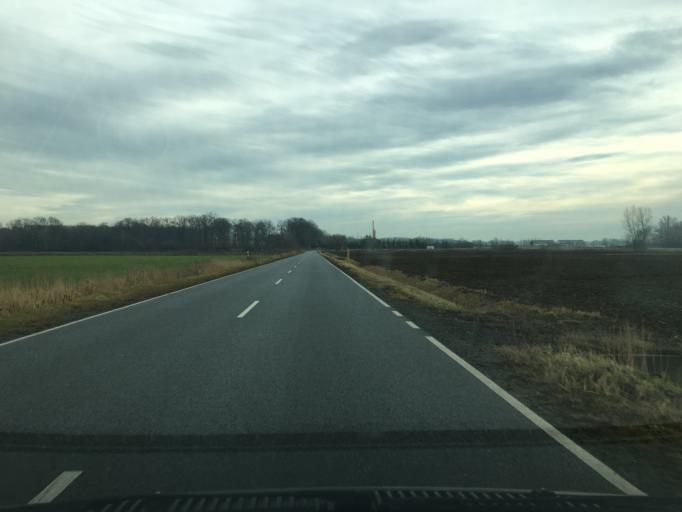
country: PL
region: Lower Silesian Voivodeship
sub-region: Powiat wroclawski
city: Dlugoleka
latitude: 51.1740
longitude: 17.2226
